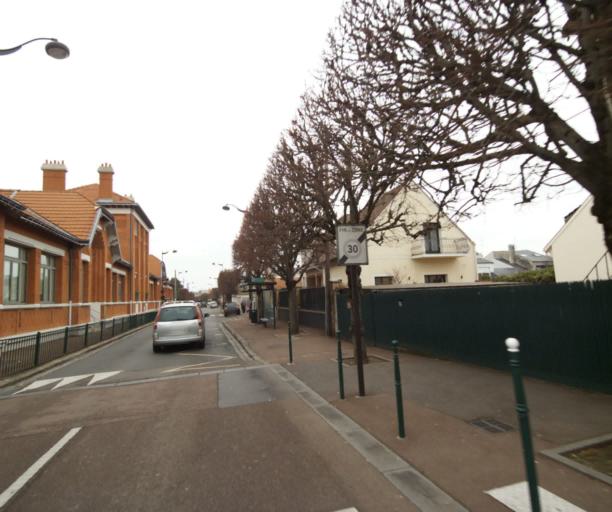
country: FR
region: Ile-de-France
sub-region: Departement des Hauts-de-Seine
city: Rueil-Malmaison
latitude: 48.8623
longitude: 2.1963
